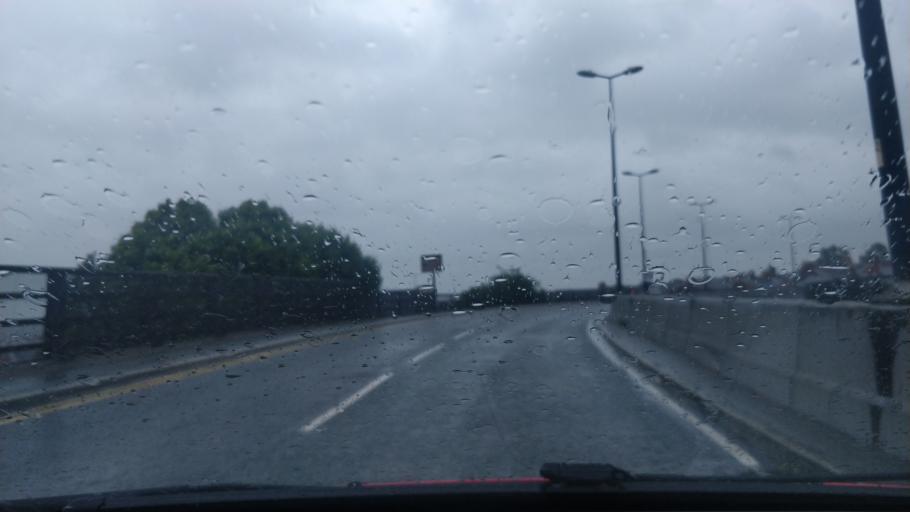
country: GB
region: England
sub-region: Cheshire West and Chester
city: Chester
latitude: 53.1941
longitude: -2.8966
